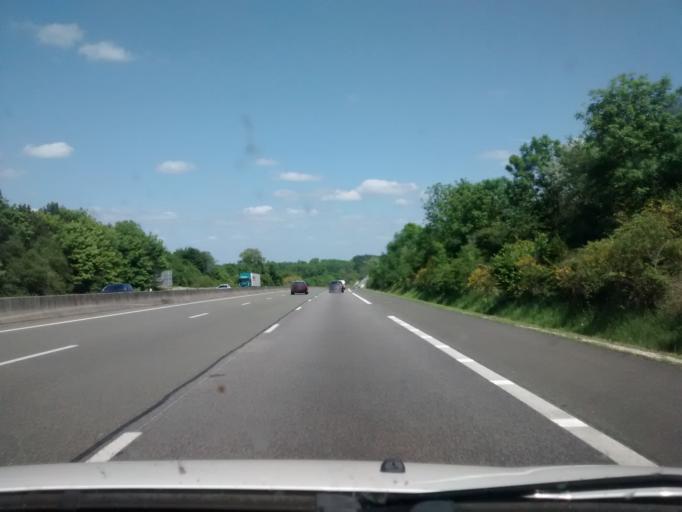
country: FR
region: Centre
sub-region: Departement d'Eure-et-Loir
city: Gallardon
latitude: 48.5042
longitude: 1.7071
